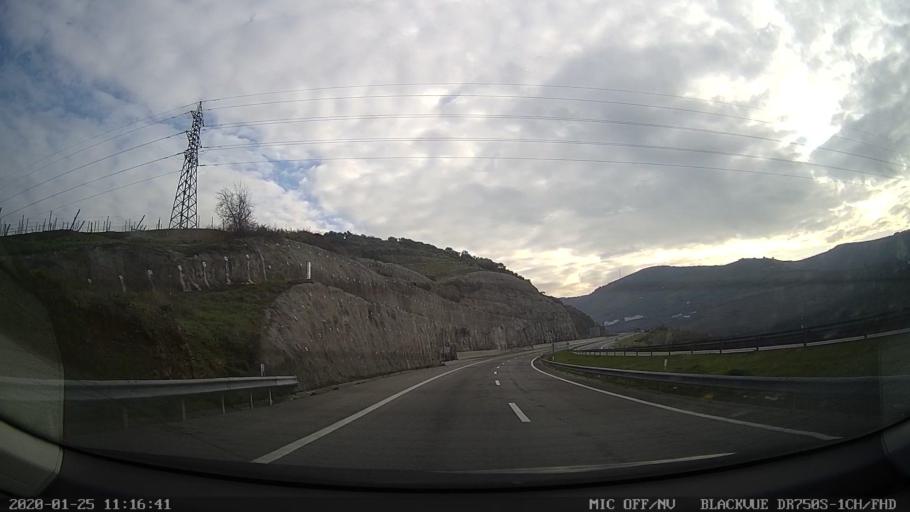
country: PT
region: Vila Real
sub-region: Peso da Regua
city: Peso da Regua
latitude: 41.1751
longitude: -7.7622
